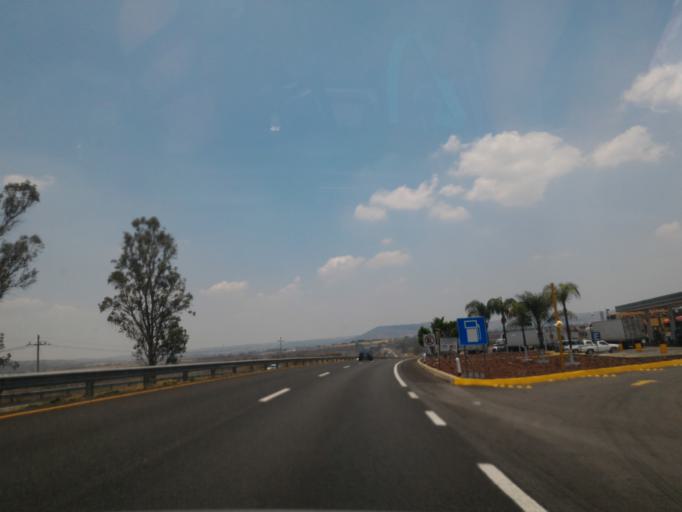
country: MX
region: Jalisco
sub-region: Tonala
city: Mismaloya (Fraccionamiento Pedregal de Santa Martha)
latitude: 20.6082
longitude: -103.1295
